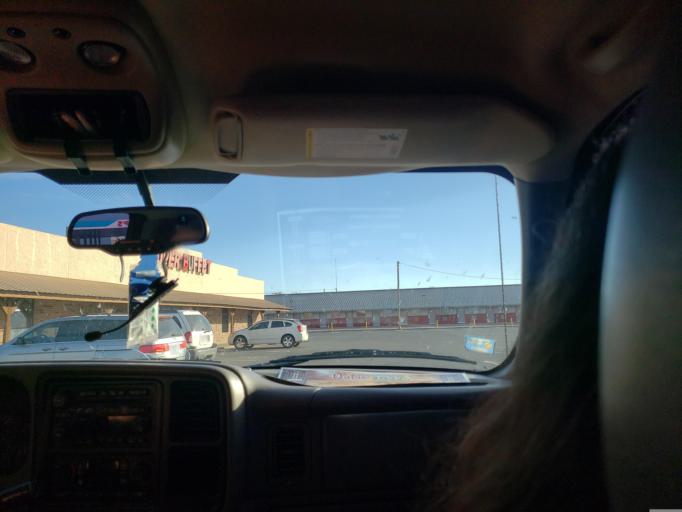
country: US
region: Oklahoma
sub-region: Texas County
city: Guymon
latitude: 36.6880
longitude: -101.4670
